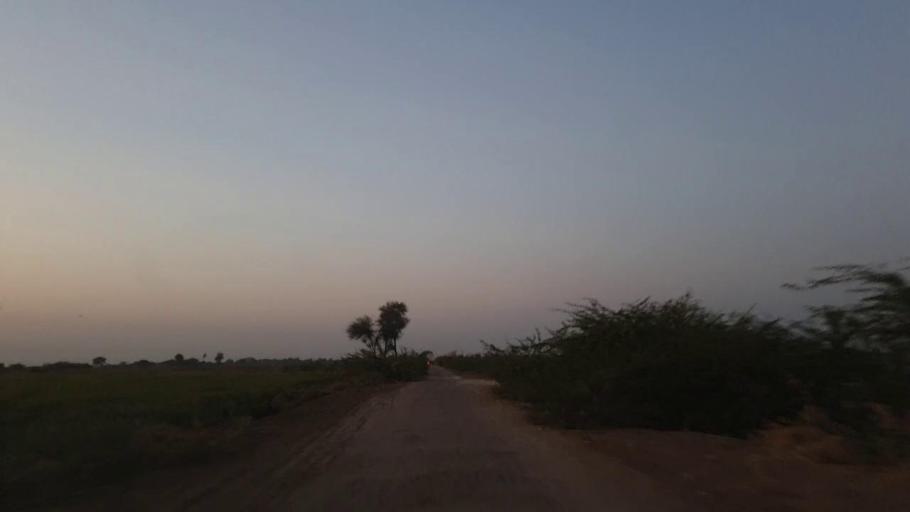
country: PK
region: Sindh
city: Naukot
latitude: 24.8991
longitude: 69.3809
